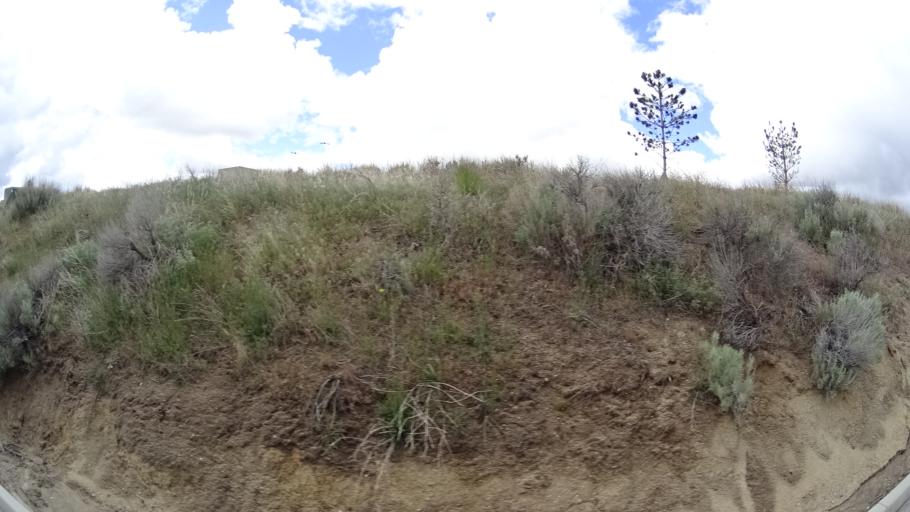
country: US
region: Idaho
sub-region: Ada County
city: Boise
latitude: 43.7022
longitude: -116.1646
